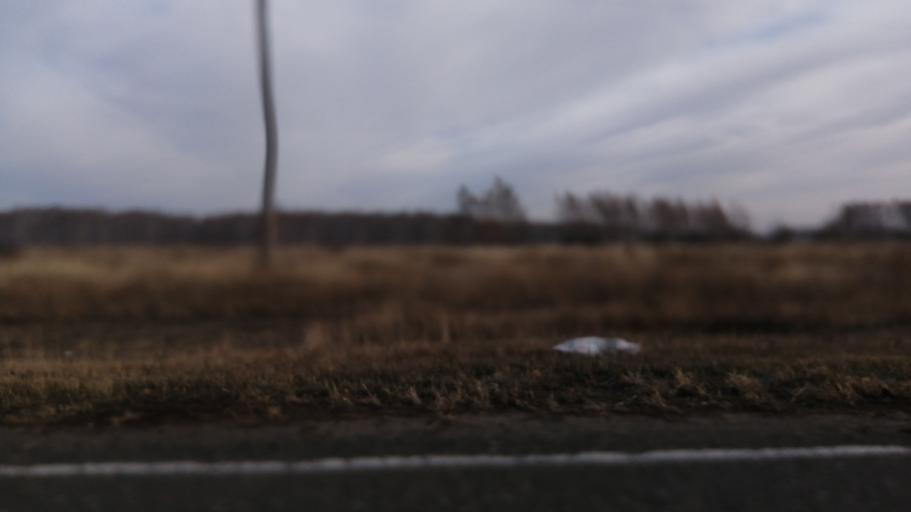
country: RU
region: Novosibirsk
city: Krasnozerskoye
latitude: 53.9865
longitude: 78.7360
